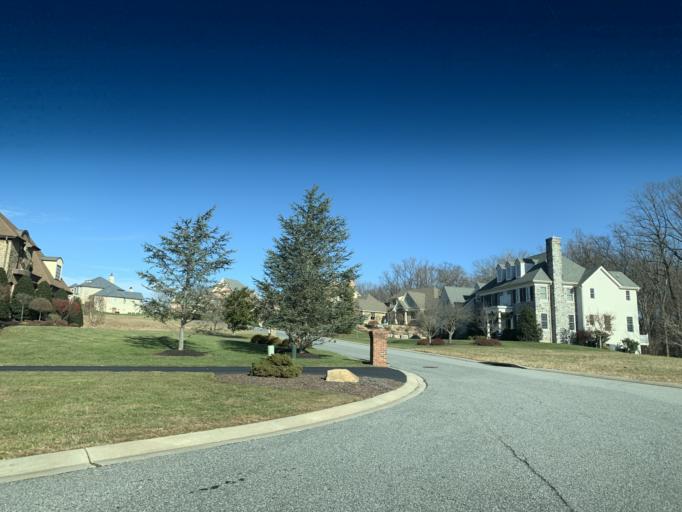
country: US
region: Maryland
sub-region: Harford County
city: Bel Air South
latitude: 39.5107
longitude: -76.3031
